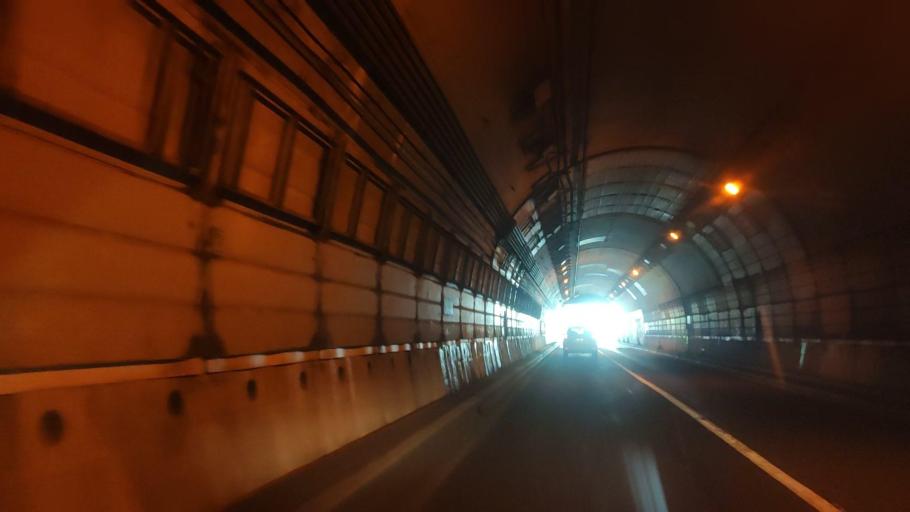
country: JP
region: Hokkaido
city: Rumoi
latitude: 43.7905
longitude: 141.3726
